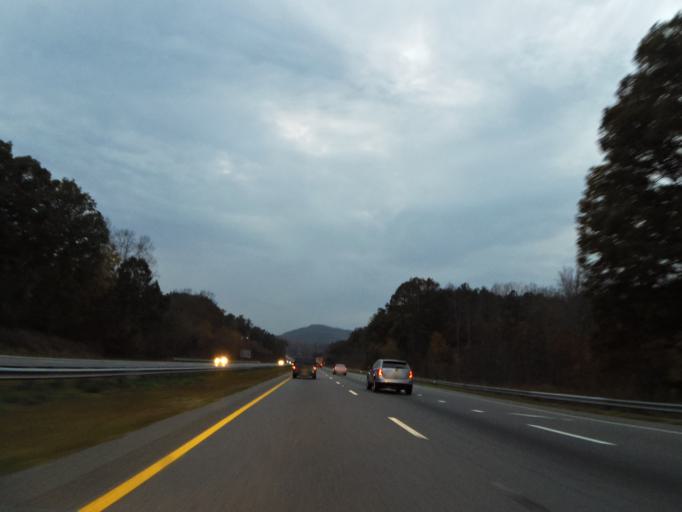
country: US
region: North Carolina
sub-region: McDowell County
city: Marion
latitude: 35.6846
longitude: -81.9168
